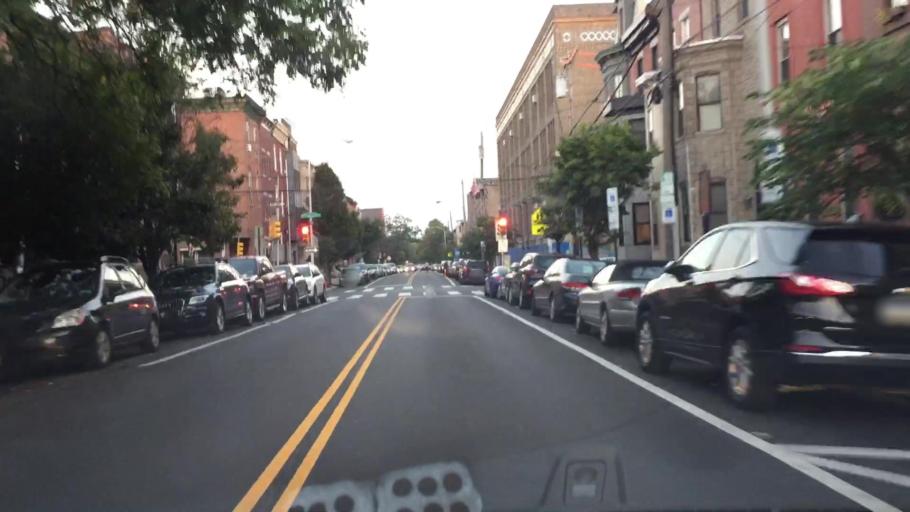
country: US
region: Pennsylvania
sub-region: Philadelphia County
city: Philadelphia
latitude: 39.9407
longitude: -75.1718
